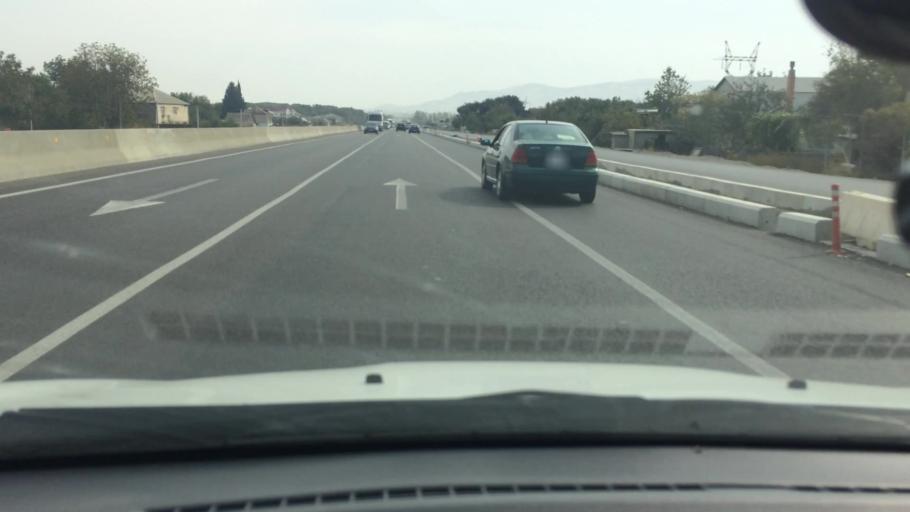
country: GE
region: T'bilisi
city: Tbilisi
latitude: 41.6364
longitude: 44.9167
